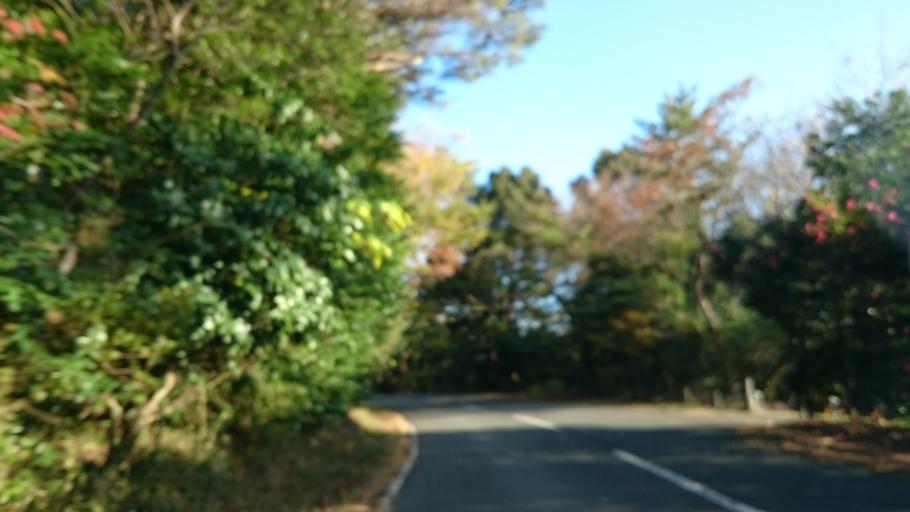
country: JP
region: Shizuoka
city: Heda
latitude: 34.9759
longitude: 138.8887
